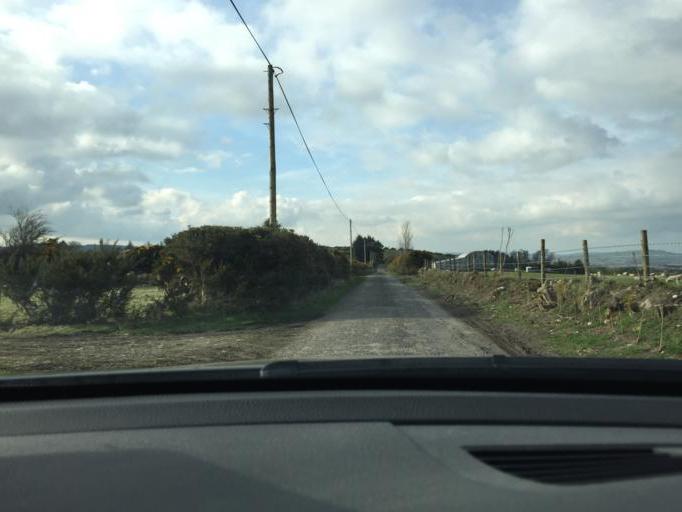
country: IE
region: Leinster
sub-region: Wicklow
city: Valleymount
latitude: 53.0839
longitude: -6.5192
